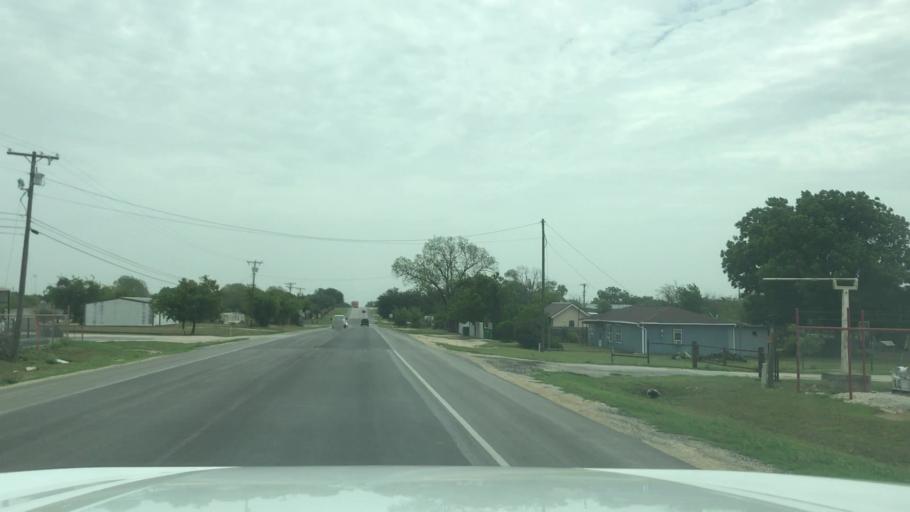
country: US
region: Texas
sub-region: Erath County
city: Dublin
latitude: 32.0835
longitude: -98.3306
